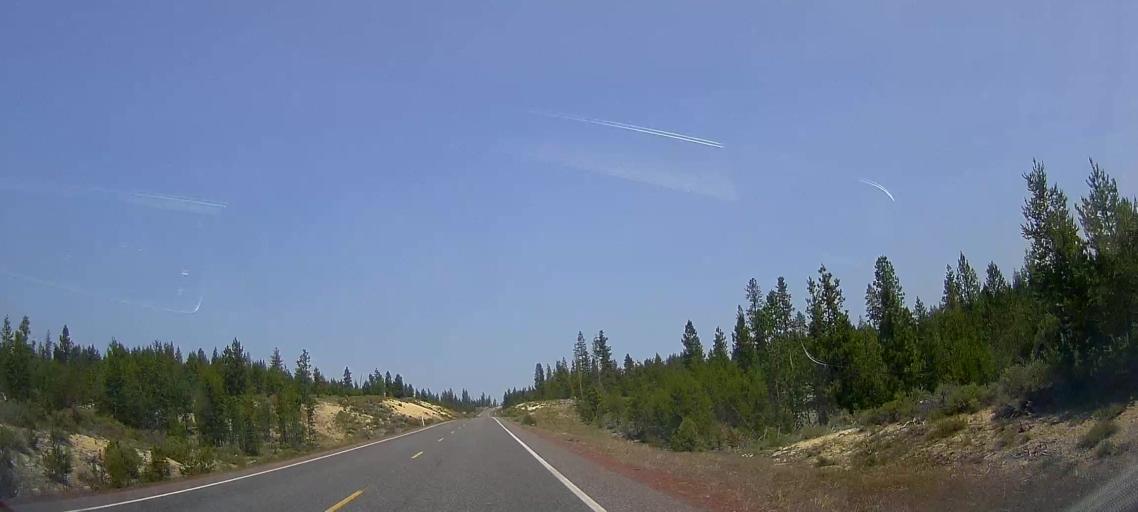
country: US
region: Oregon
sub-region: Deschutes County
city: La Pine
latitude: 43.4045
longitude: -121.7237
